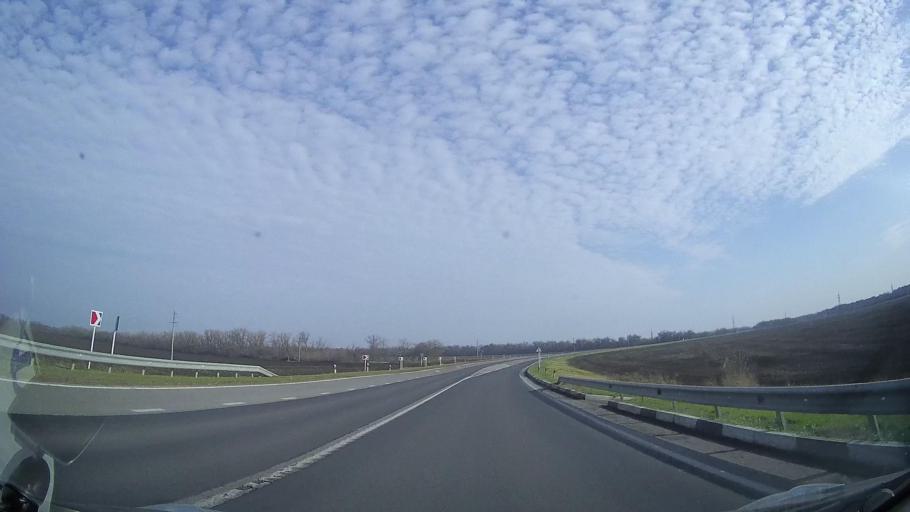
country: RU
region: Rostov
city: Tselina
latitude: 46.5320
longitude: 41.1725
